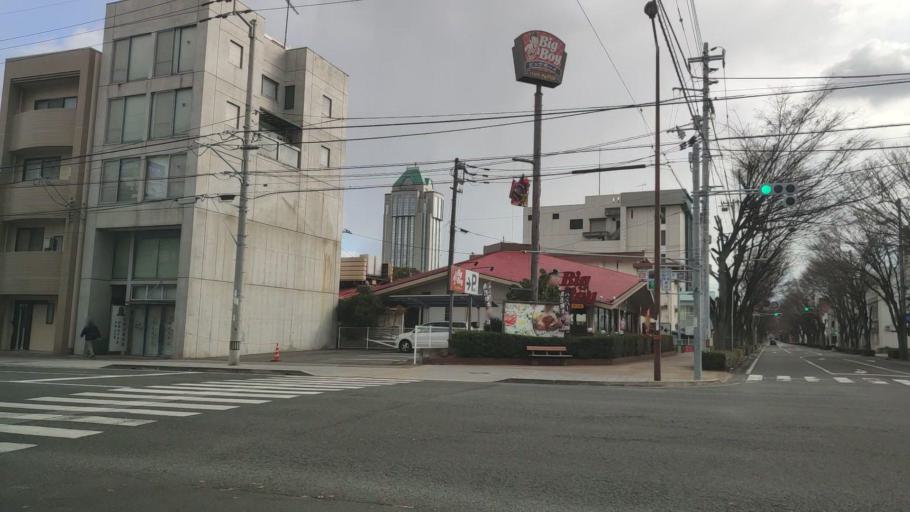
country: JP
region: Ehime
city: Hojo
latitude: 34.0631
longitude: 132.9965
